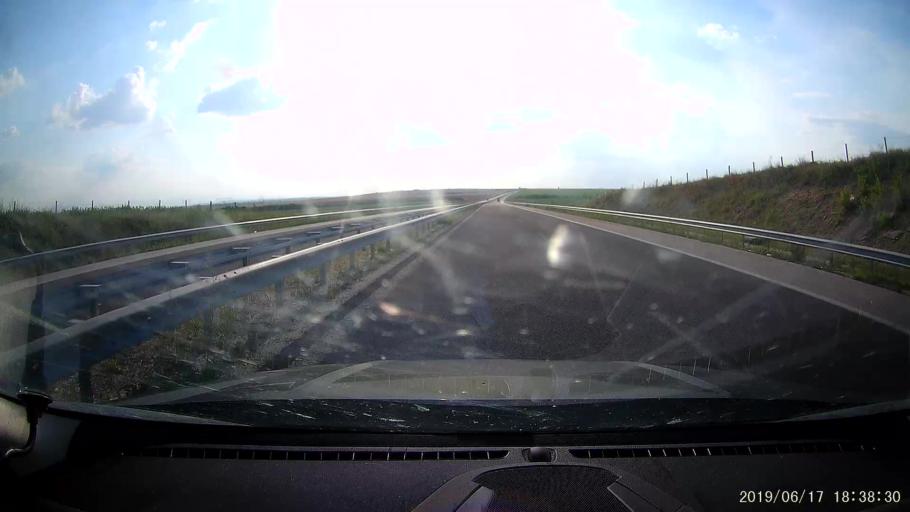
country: BG
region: Stara Zagora
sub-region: Obshtina Chirpan
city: Chirpan
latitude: 42.1373
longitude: 25.3351
